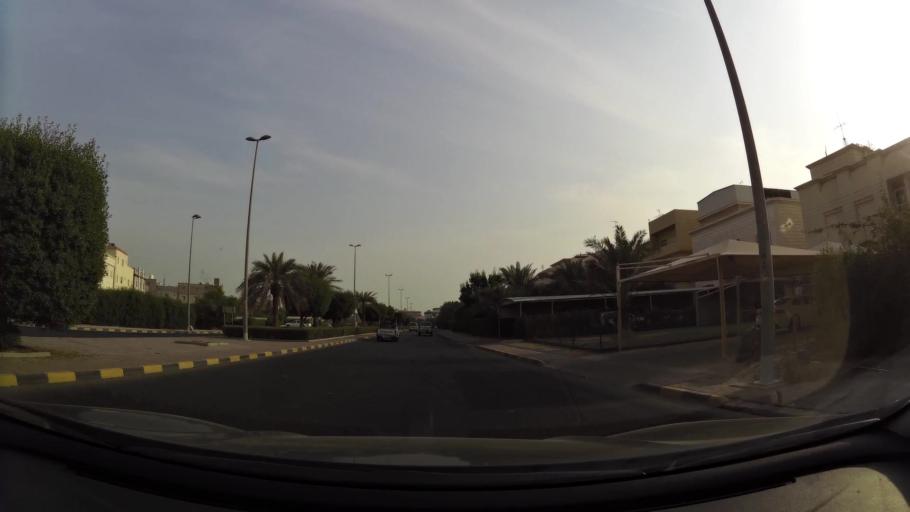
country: KW
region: Mubarak al Kabir
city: Sabah as Salim
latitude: 29.2199
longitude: 48.0617
